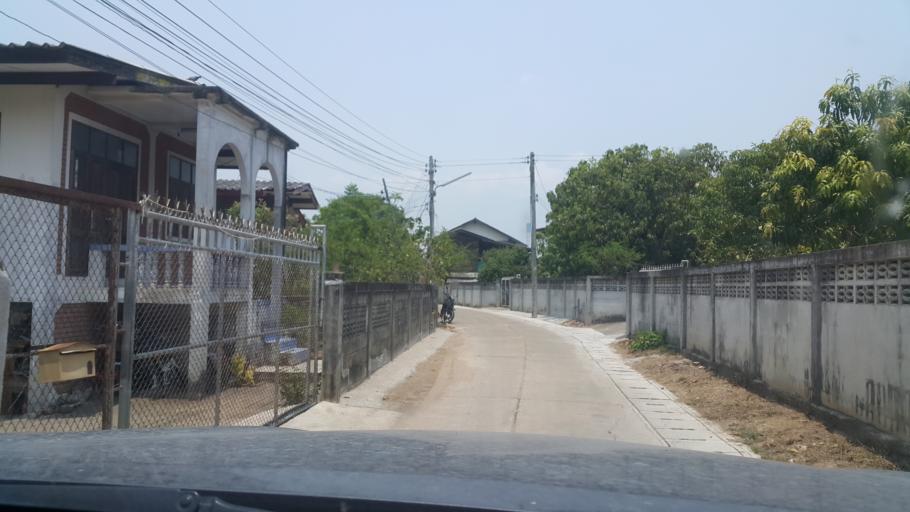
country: TH
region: Lampang
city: Thoen
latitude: 17.6389
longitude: 99.2380
